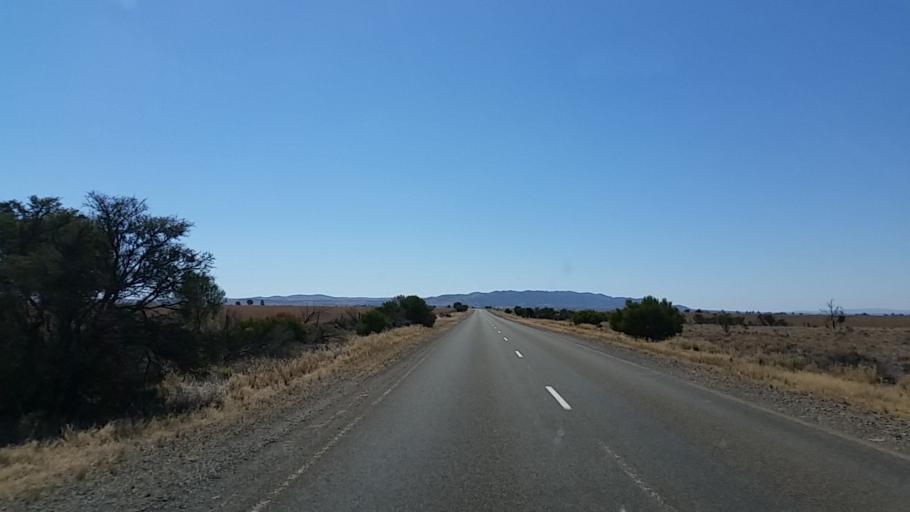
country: AU
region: South Australia
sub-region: Peterborough
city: Peterborough
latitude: -32.6731
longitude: 138.6079
